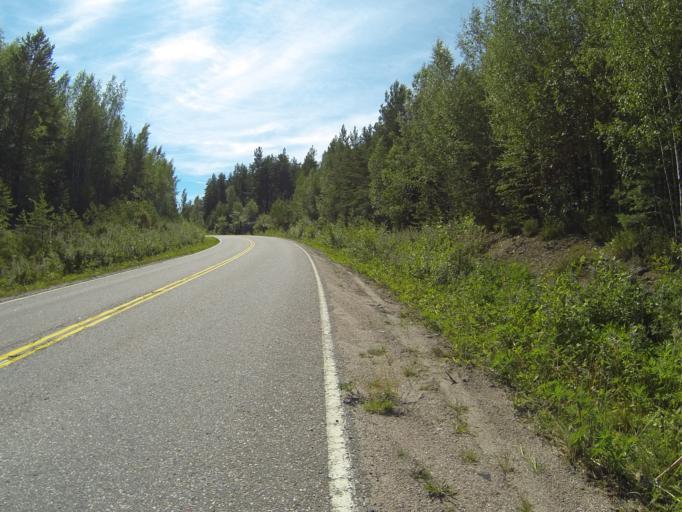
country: FI
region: Varsinais-Suomi
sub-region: Salo
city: Saerkisalo
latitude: 60.2678
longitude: 22.9725
